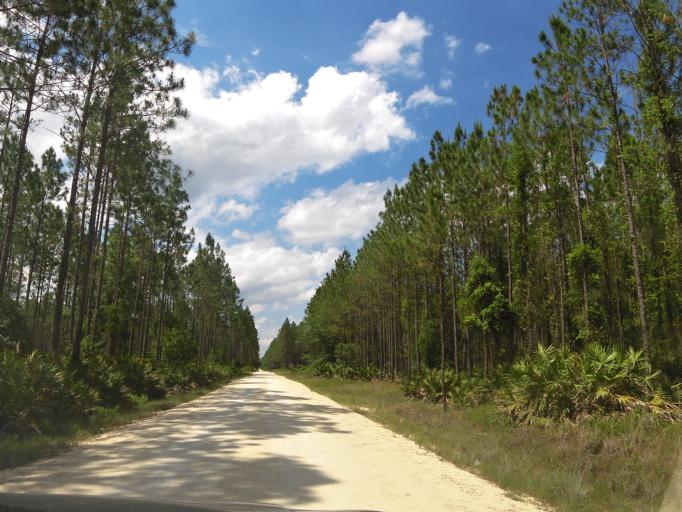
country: US
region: Florida
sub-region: Clay County
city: Asbury Lake
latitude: 29.8713
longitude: -81.8532
